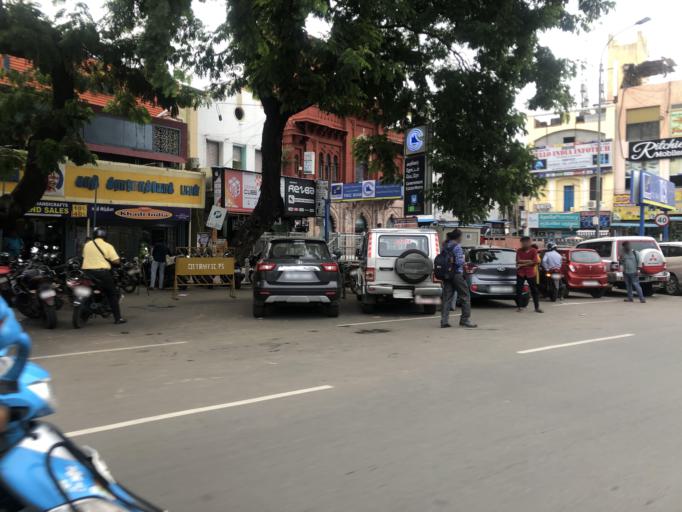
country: IN
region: Tamil Nadu
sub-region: Chennai
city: Chennai
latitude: 13.0693
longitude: 80.2722
